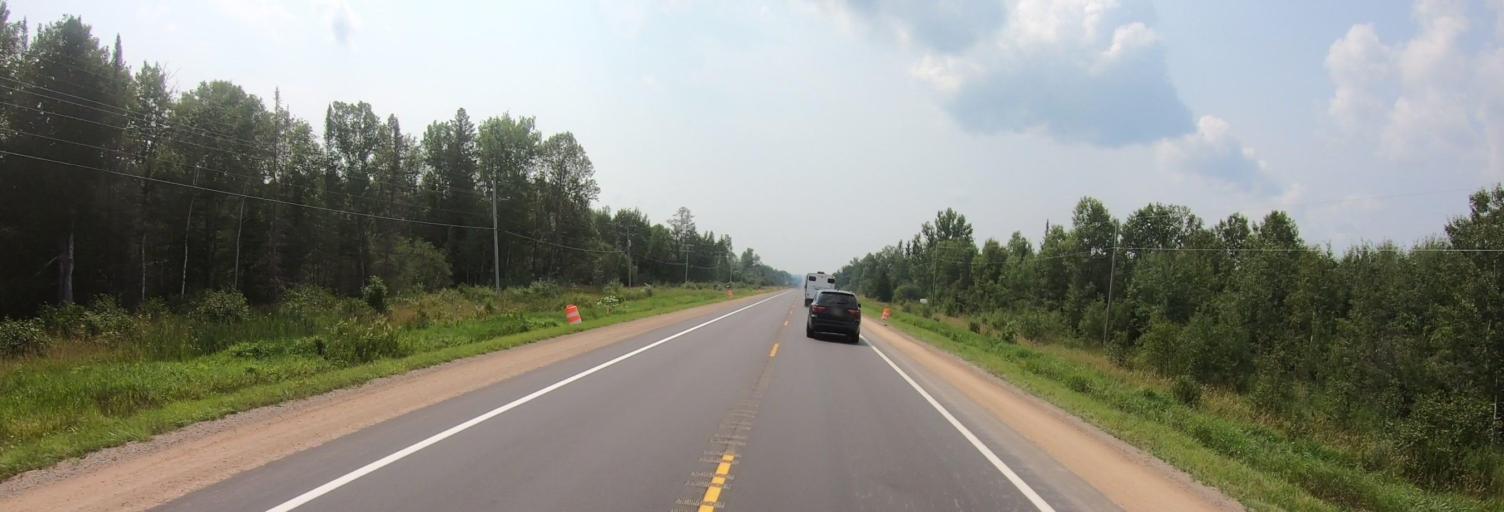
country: US
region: Michigan
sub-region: Luce County
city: Newberry
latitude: 46.3950
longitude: -85.5099
